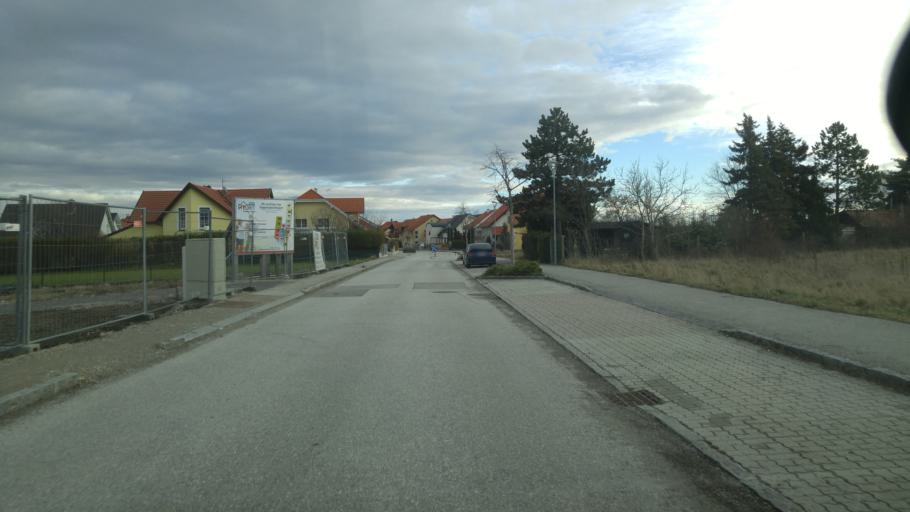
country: AT
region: Lower Austria
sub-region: Politischer Bezirk Baden
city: Bad Voslau
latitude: 47.9585
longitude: 16.2100
